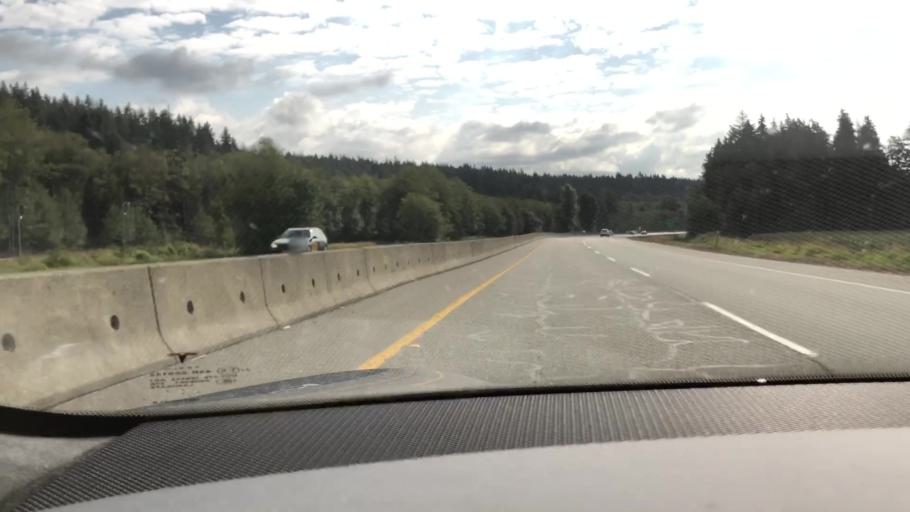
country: CA
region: British Columbia
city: Delta
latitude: 49.1144
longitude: -122.9156
